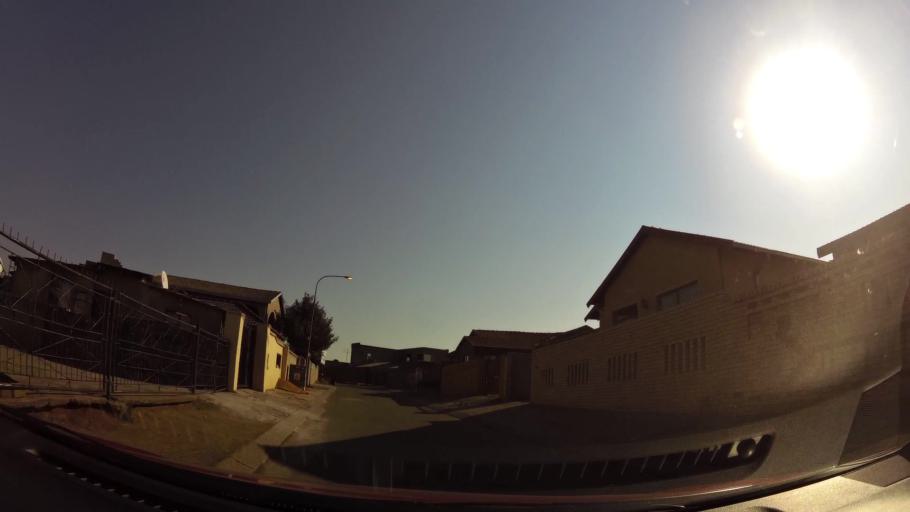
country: ZA
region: Gauteng
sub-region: City of Johannesburg Metropolitan Municipality
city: Soweto
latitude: -26.2466
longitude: 27.9500
